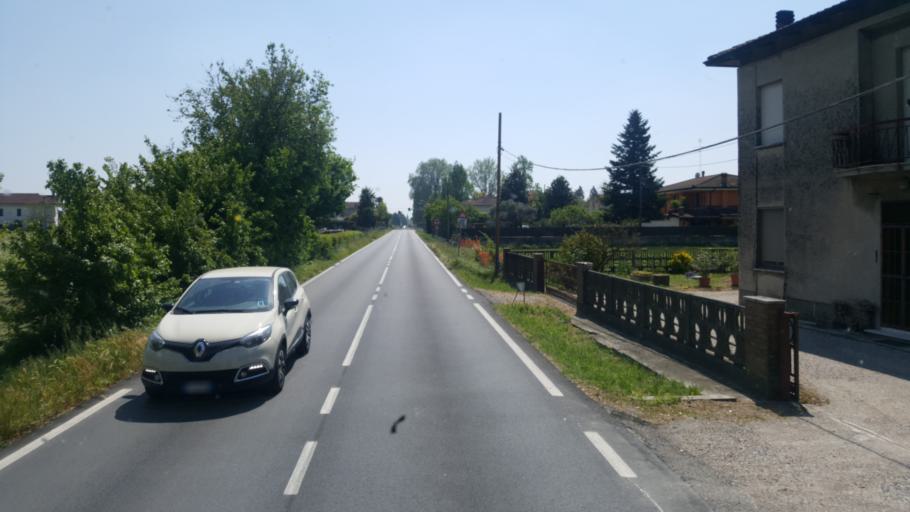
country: IT
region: Lombardy
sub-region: Provincia di Mantova
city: San Benedetto Po
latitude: 45.0580
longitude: 10.9309
